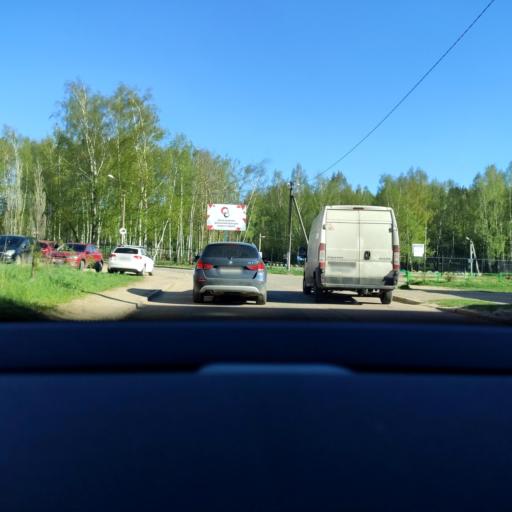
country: RU
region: Moskovskaya
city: Dmitrov
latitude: 56.3577
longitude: 37.5652
